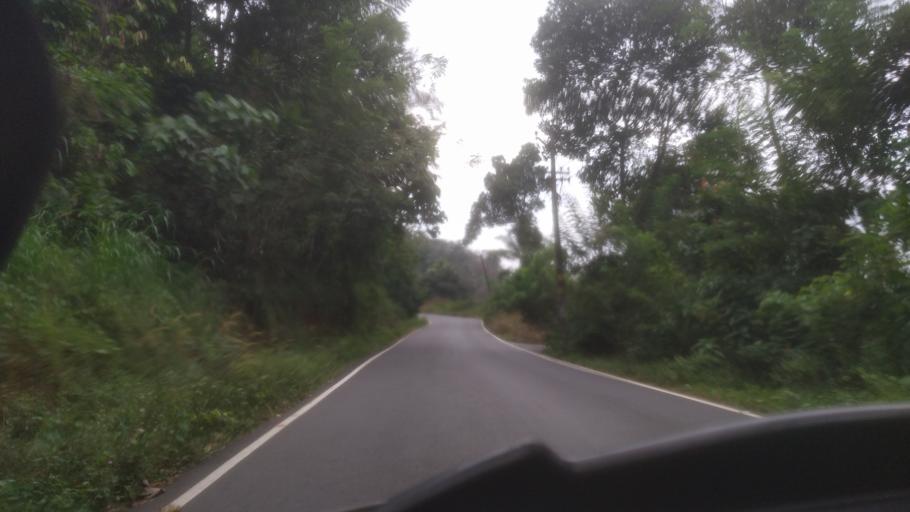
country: IN
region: Kerala
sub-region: Idukki
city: Idukki
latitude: 9.9723
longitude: 76.9988
